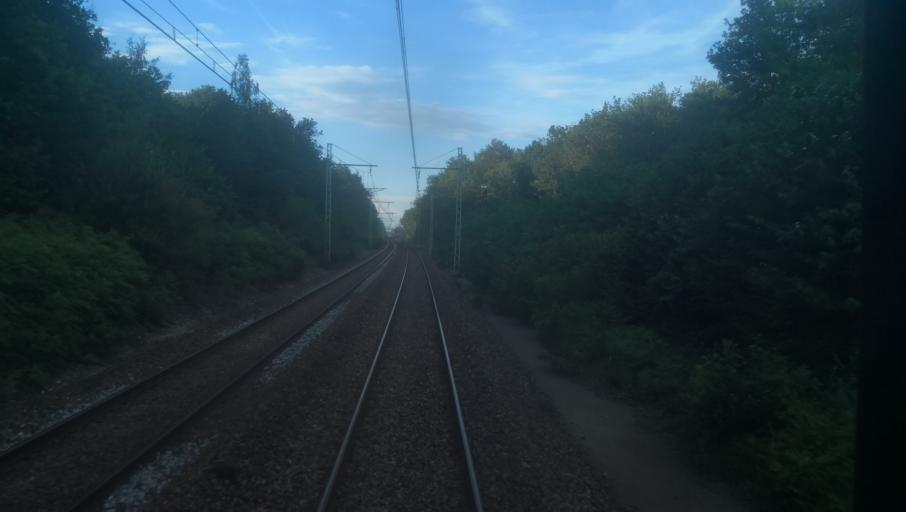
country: FR
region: Centre
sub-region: Departement de l'Indre
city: Luant
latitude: 46.6883
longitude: 1.5585
